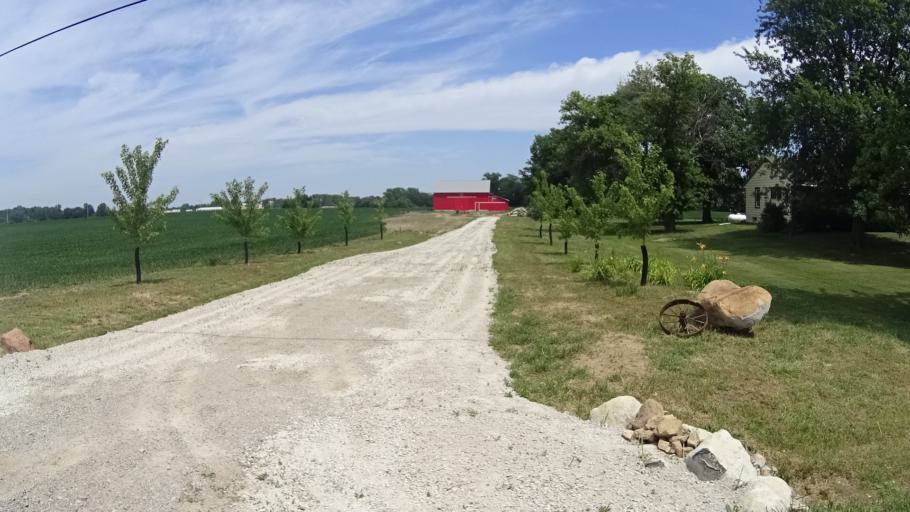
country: US
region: Ohio
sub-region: Erie County
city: Sandusky
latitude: 41.3951
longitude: -82.7709
